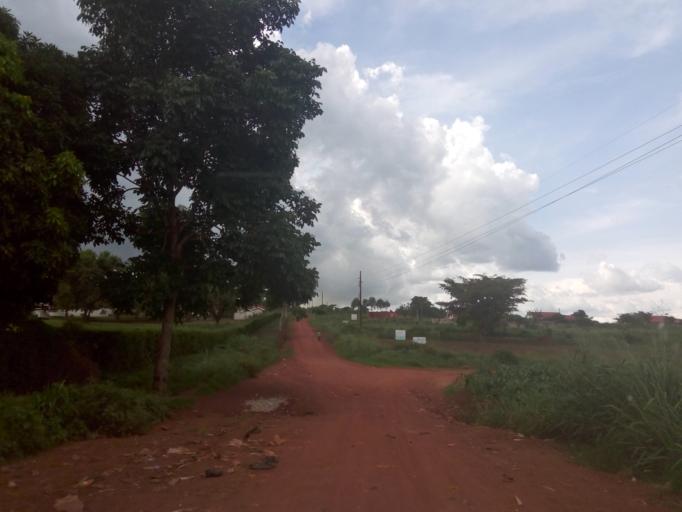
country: UG
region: Western Region
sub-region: Masindi District
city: Masindi
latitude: 1.6838
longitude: 31.7240
